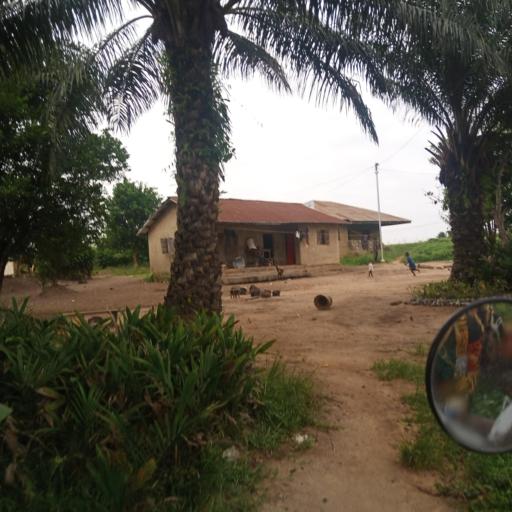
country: SL
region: Eastern Province
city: Pendembu
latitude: 8.0926
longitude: -10.6914
